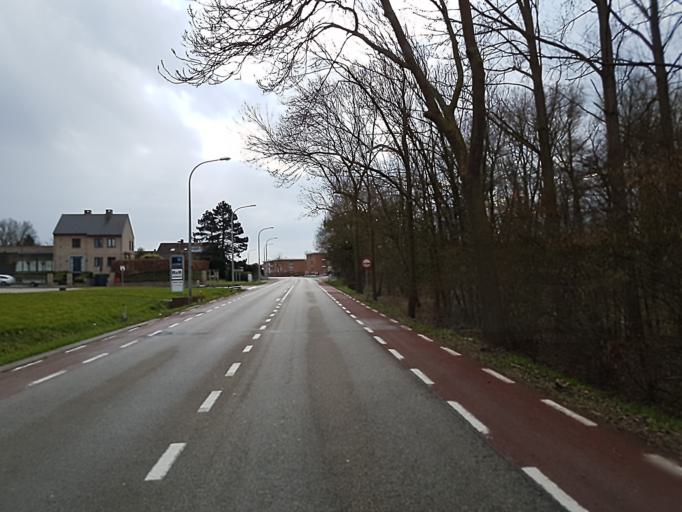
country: BE
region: Flanders
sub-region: Provincie Limburg
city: Tongeren
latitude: 50.7913
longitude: 5.4507
